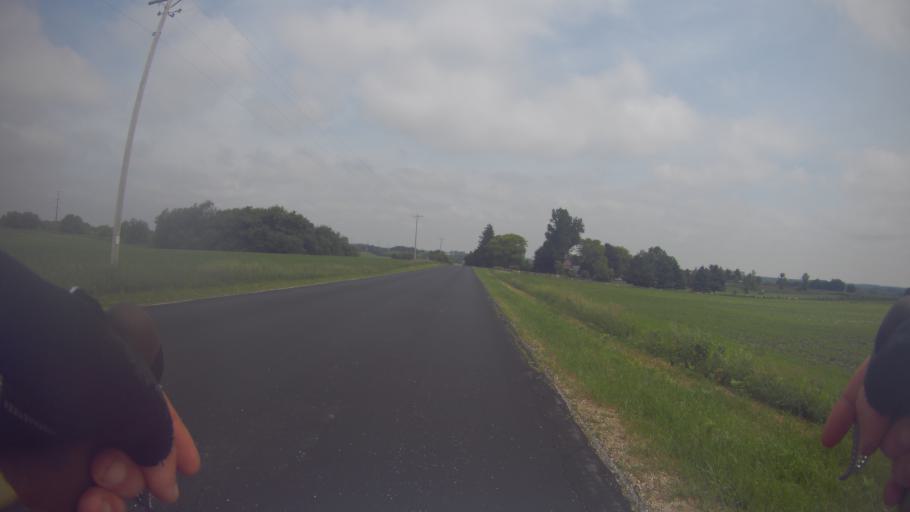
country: US
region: Wisconsin
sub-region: Rock County
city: Edgerton
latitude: 42.9100
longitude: -89.0427
